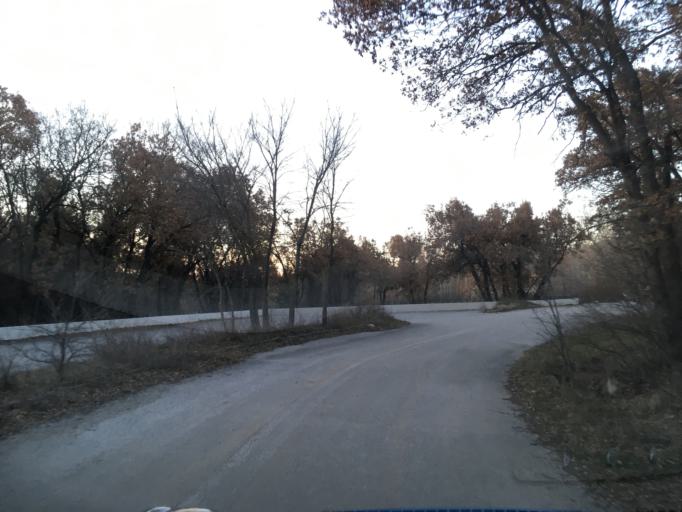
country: GR
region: West Macedonia
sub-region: Nomos Kozanis
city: Koila
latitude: 40.3303
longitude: 21.8320
